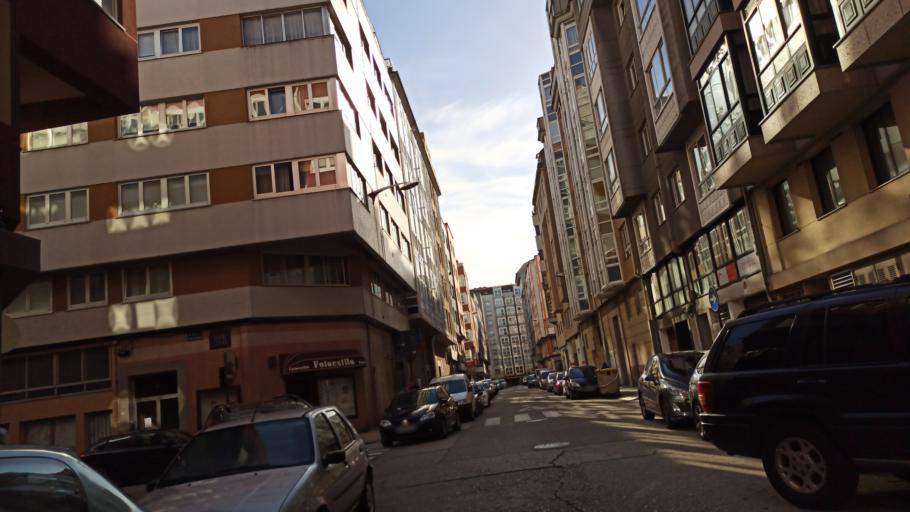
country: ES
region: Galicia
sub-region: Provincia da Coruna
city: A Coruna
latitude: 43.3601
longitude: -8.4221
